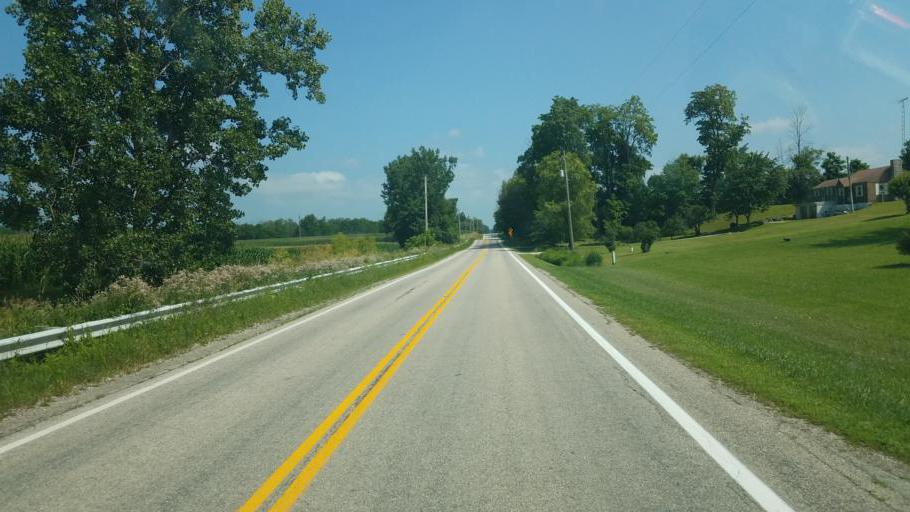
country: US
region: Ohio
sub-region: Crawford County
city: Galion
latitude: 40.8329
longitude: -82.8556
